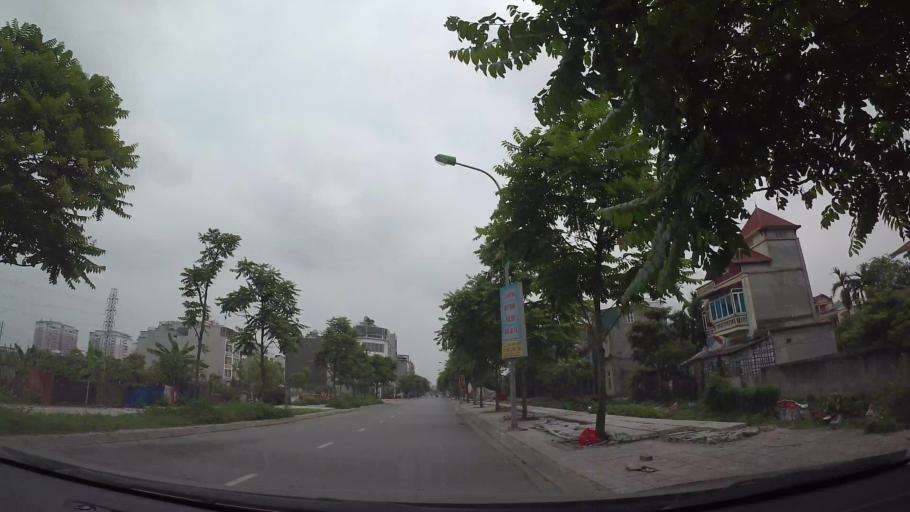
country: VN
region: Ha Noi
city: Trau Quy
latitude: 21.0595
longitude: 105.9012
